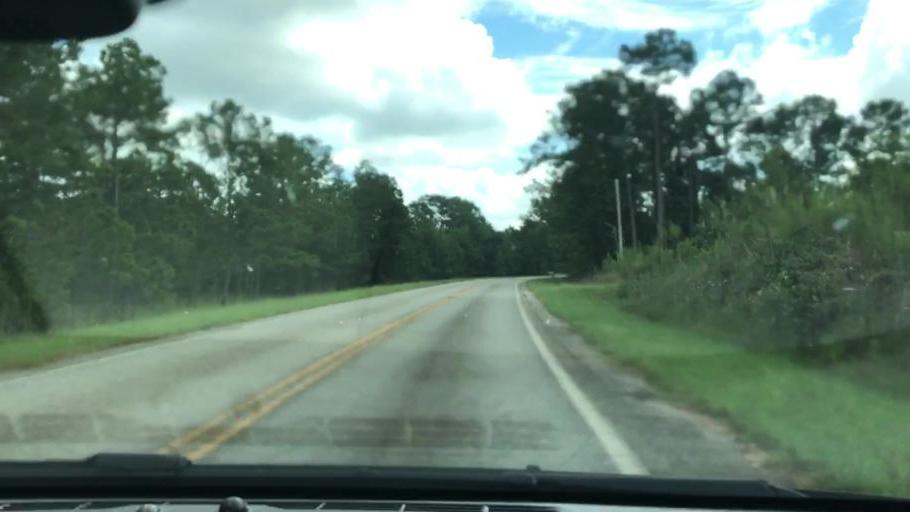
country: US
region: Georgia
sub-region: Stewart County
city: Lumpkin
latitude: 32.0707
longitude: -84.8445
